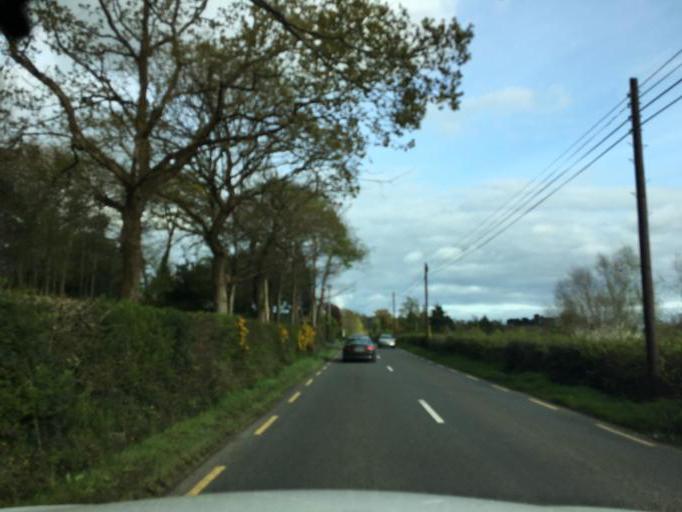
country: IE
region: Leinster
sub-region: Loch Garman
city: New Ross
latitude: 52.4236
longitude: -6.9375
